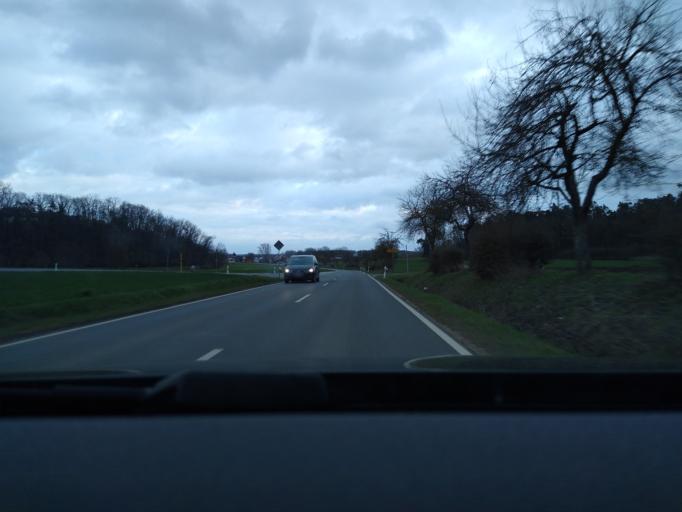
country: DE
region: Bavaria
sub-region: Regierungsbezirk Mittelfranken
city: Zirndorf
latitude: 49.4546
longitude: 10.9181
